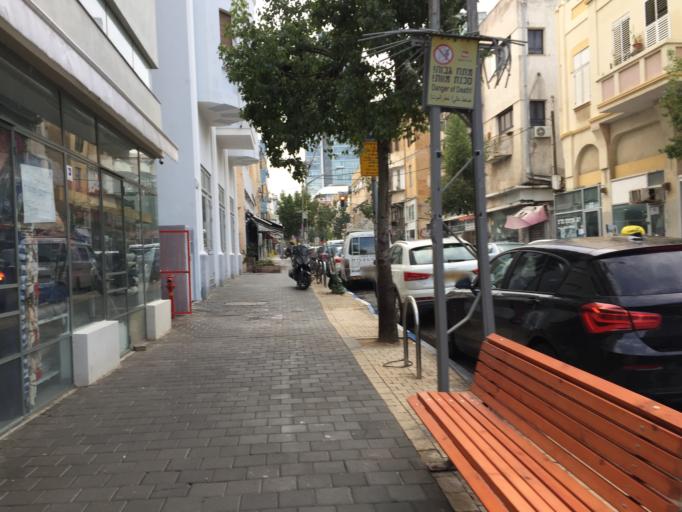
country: IL
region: Tel Aviv
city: Tel Aviv
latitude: 32.0657
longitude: 34.7706
